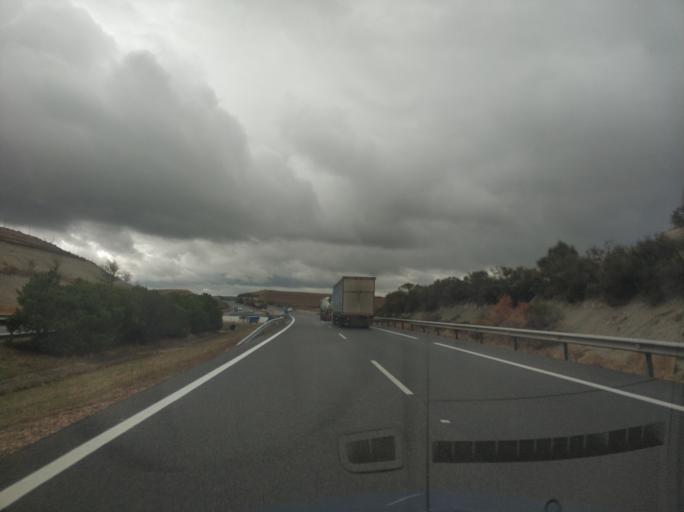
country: ES
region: Castille and Leon
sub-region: Provincia de Palencia
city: Soto de Cerrato
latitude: 41.9671
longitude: -4.4564
